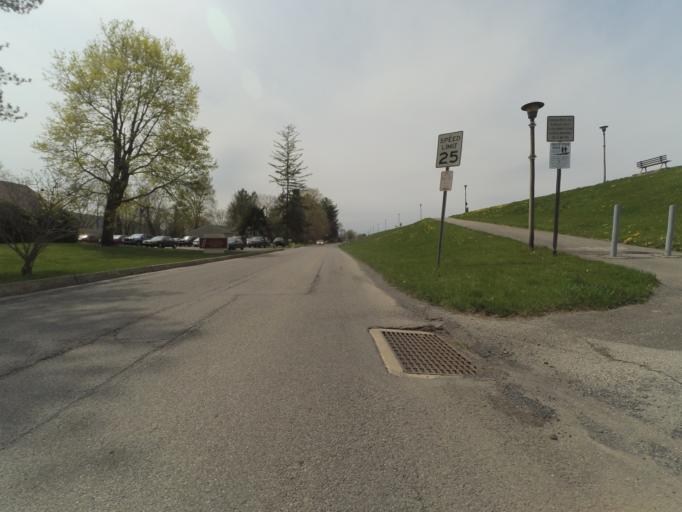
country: US
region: Pennsylvania
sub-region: Clinton County
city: Dunnstown
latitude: 41.1376
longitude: -77.4275
